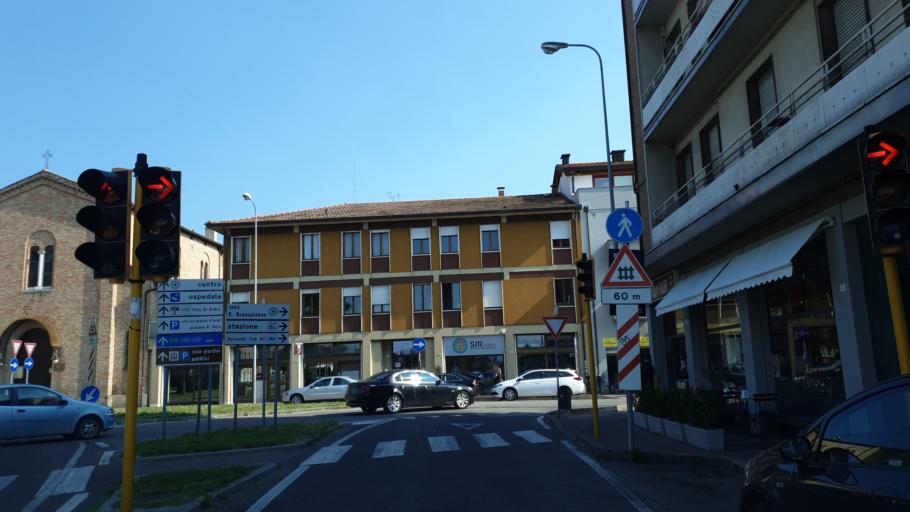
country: IT
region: Emilia-Romagna
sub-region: Provincia di Ravenna
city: Ravenna
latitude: 44.4170
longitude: 12.2095
